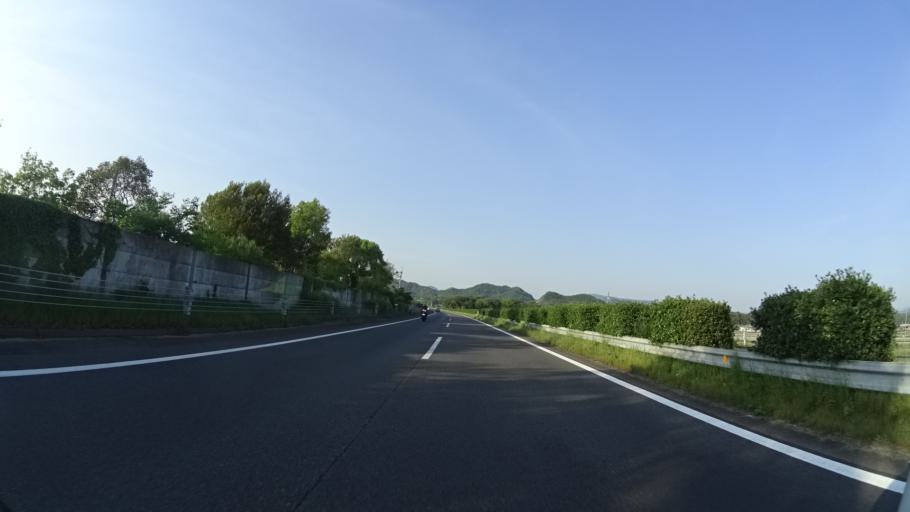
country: JP
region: Kagawa
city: Kan'onjicho
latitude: 34.1362
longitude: 133.7088
